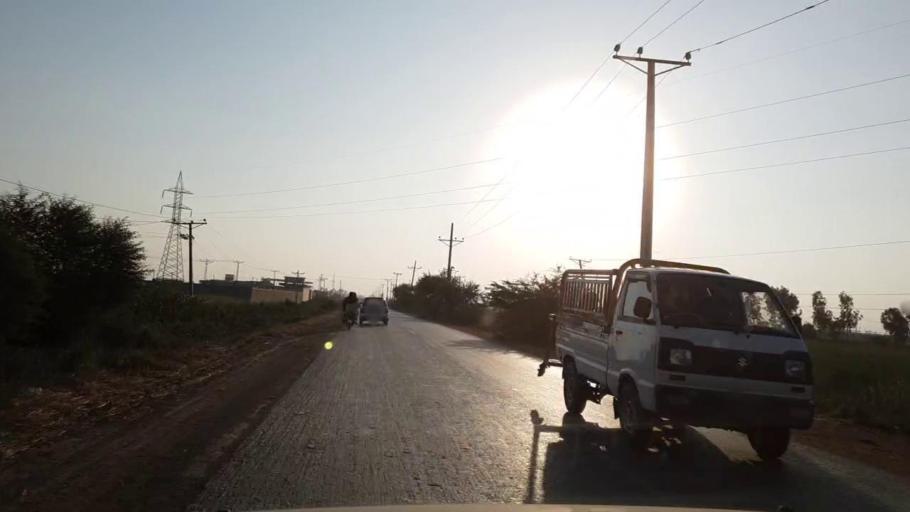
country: PK
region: Sindh
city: Daro Mehar
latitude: 24.6169
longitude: 68.0919
